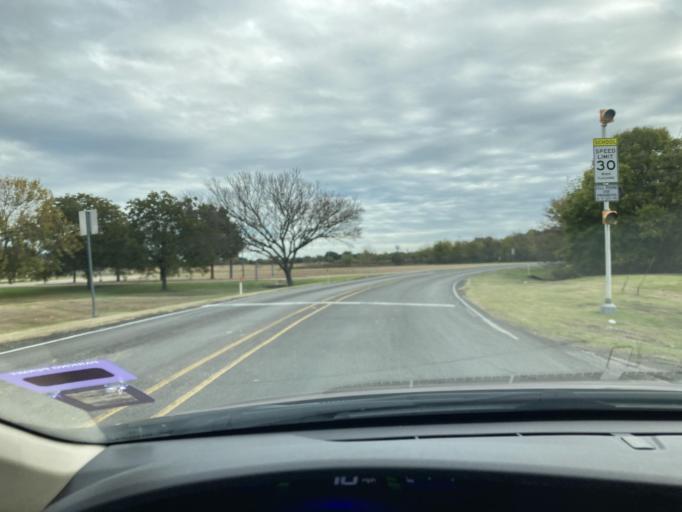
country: US
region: Texas
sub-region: Navarro County
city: Corsicana
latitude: 32.0689
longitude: -96.5020
